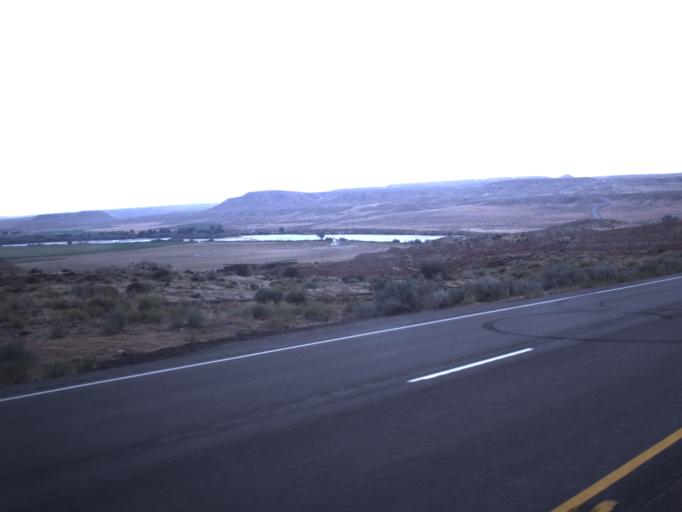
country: US
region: Utah
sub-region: Uintah County
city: Naples
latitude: 40.3270
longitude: -109.4867
